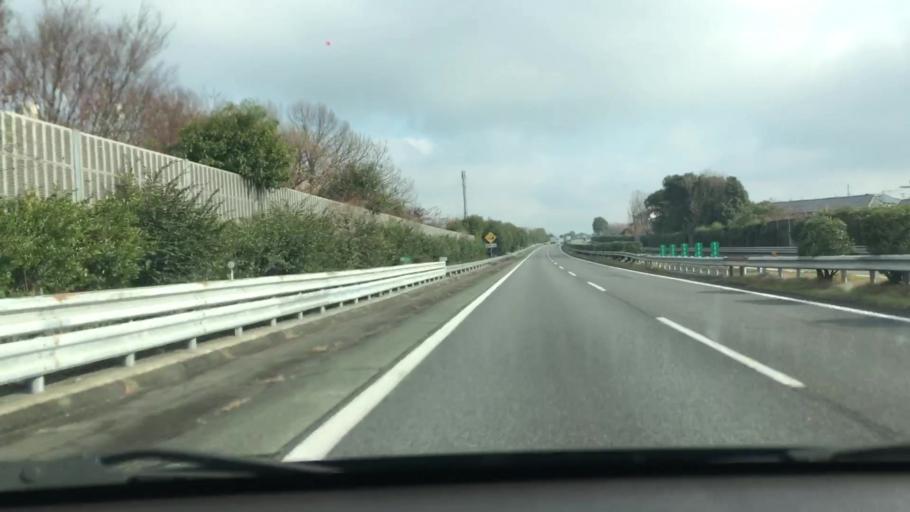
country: JP
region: Kumamoto
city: Kumamoto
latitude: 32.8571
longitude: 130.7529
